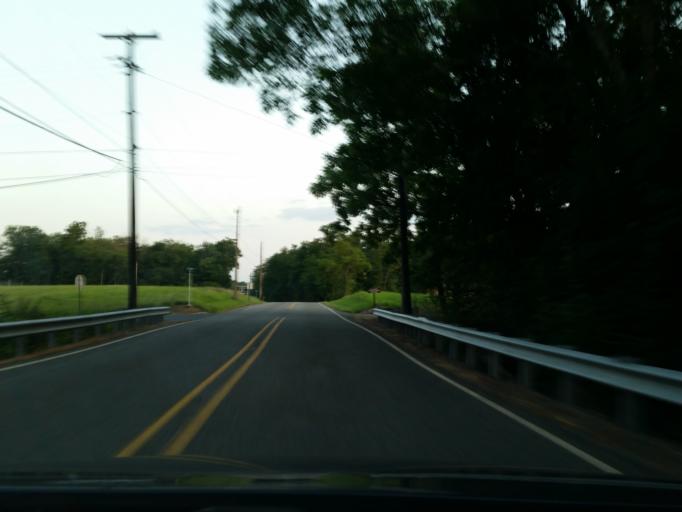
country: US
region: Pennsylvania
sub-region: Lebanon County
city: Jonestown
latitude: 40.4316
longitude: -76.5420
